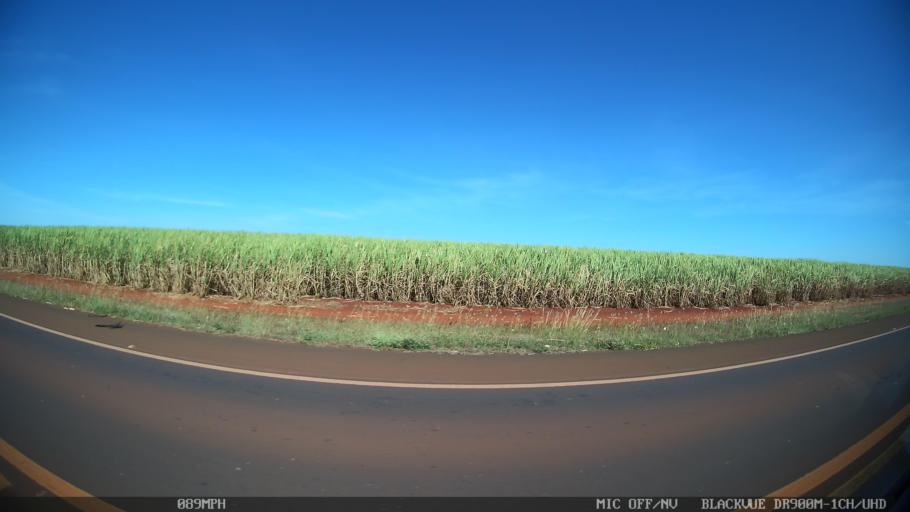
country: BR
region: Sao Paulo
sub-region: Guaira
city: Guaira
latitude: -20.4447
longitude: -48.2581
